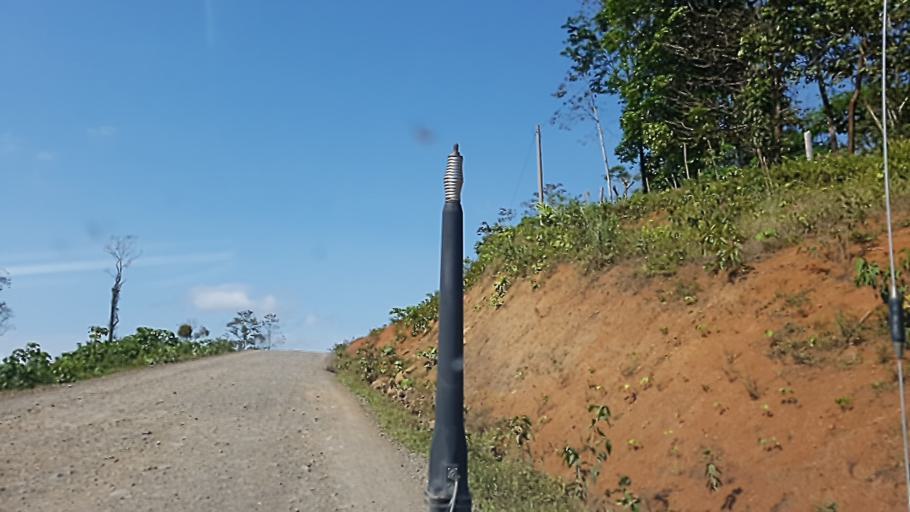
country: NI
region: Atlantico Sur
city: Nueva Guinea
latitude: 11.7868
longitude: -84.1658
